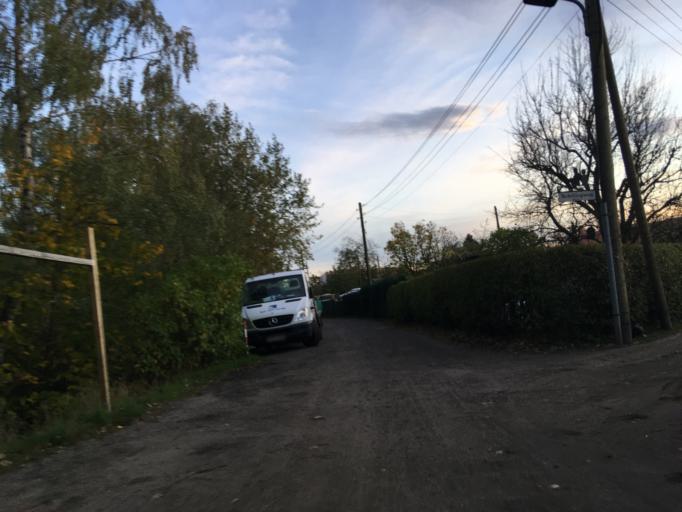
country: DE
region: Berlin
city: Buchholz
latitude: 52.6125
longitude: 13.4169
